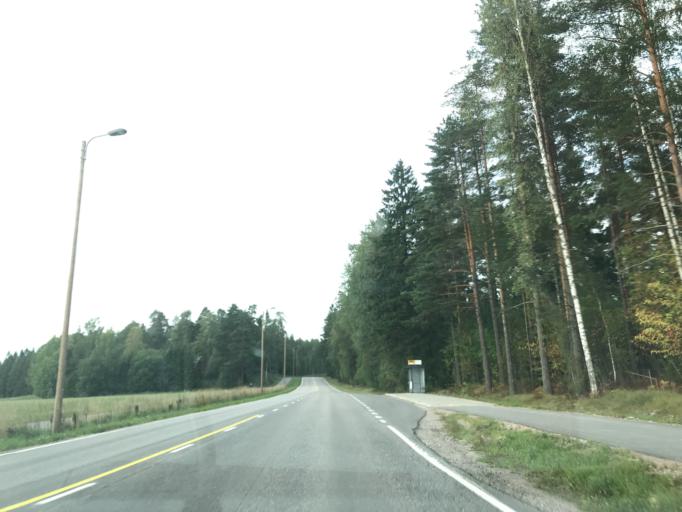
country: FI
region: Uusimaa
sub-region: Helsinki
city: Kirkkonummi
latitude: 60.2586
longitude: 24.4474
